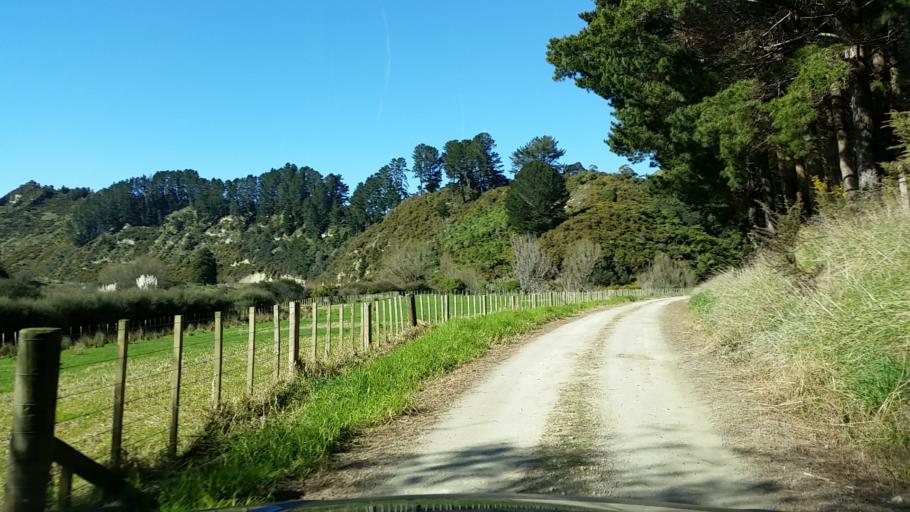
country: NZ
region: Manawatu-Wanganui
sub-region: Wanganui District
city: Wanganui
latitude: -39.6675
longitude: 174.8631
